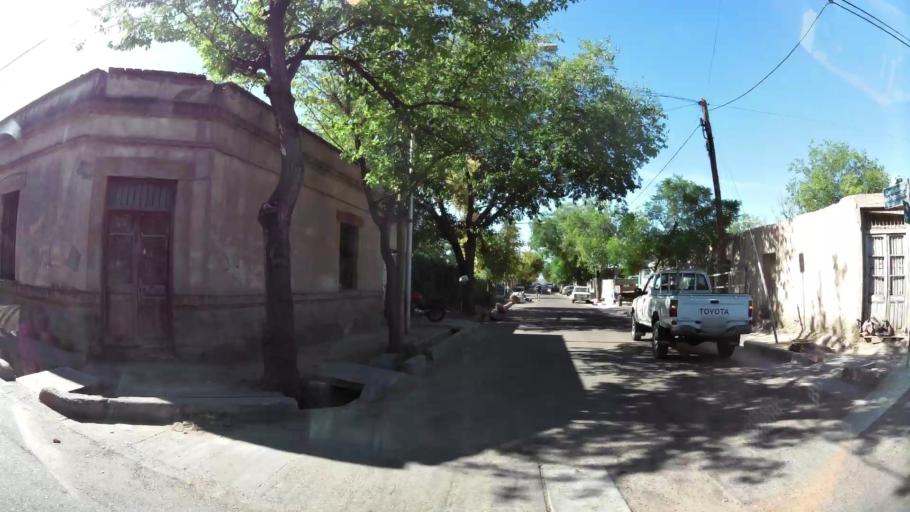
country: AR
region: Mendoza
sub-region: Departamento de Godoy Cruz
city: Godoy Cruz
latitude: -32.9415
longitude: -68.8098
